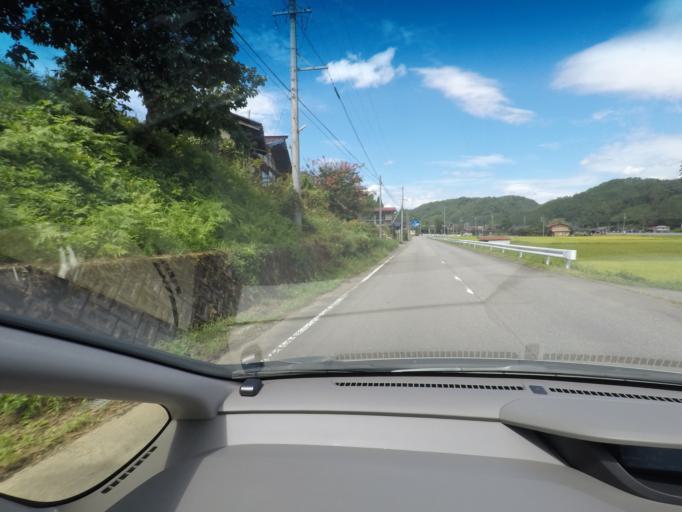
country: JP
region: Gifu
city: Takayama
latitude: 36.1340
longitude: 137.3132
